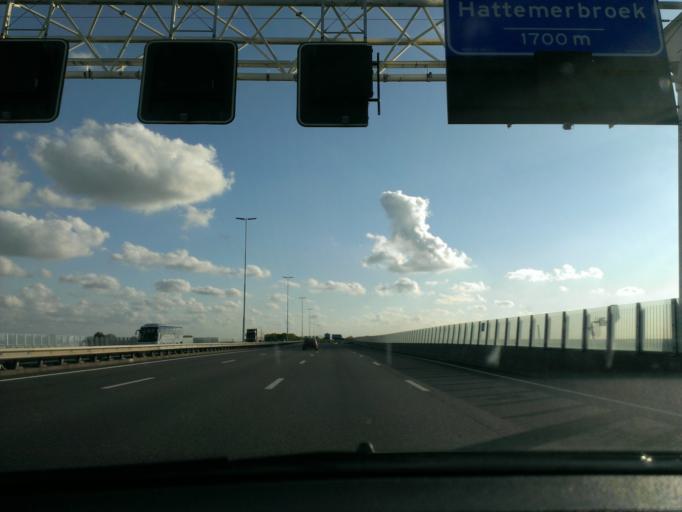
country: NL
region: Gelderland
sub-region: Gemeente Hattem
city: Hattem
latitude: 52.5005
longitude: 6.0554
